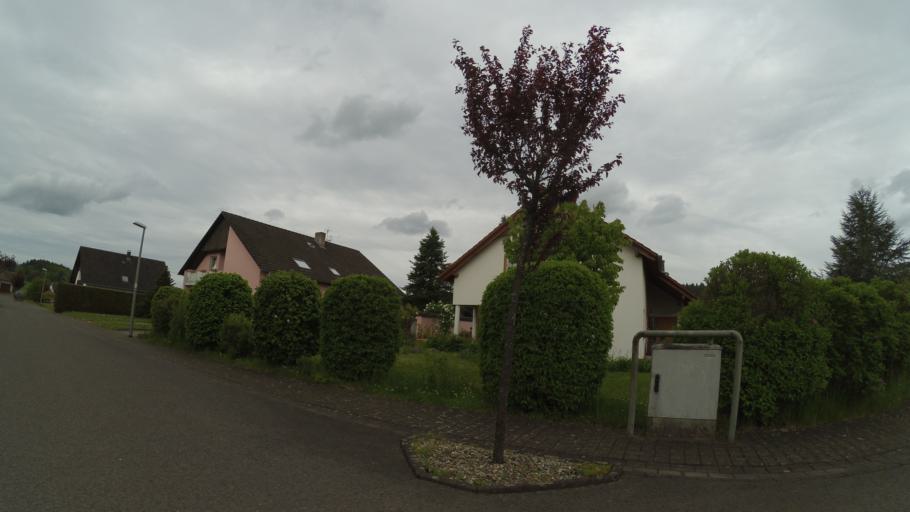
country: DE
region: Saarland
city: Saarhoelzbach
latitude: 49.5109
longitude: 6.6055
